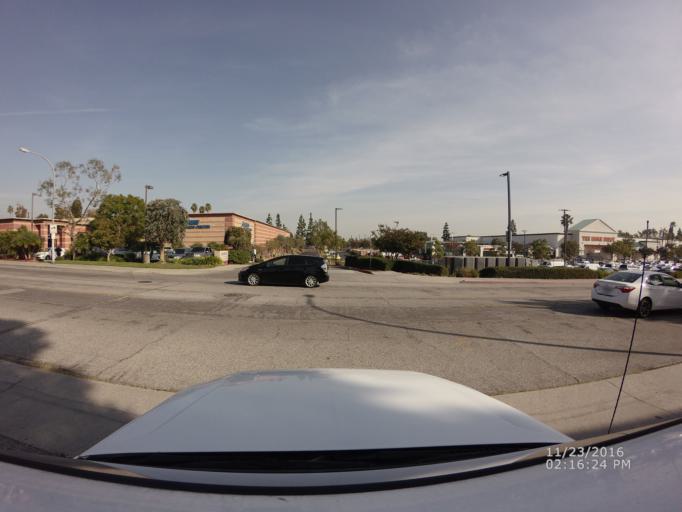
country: US
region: California
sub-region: Los Angeles County
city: Alhambra
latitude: 34.0864
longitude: -118.1422
